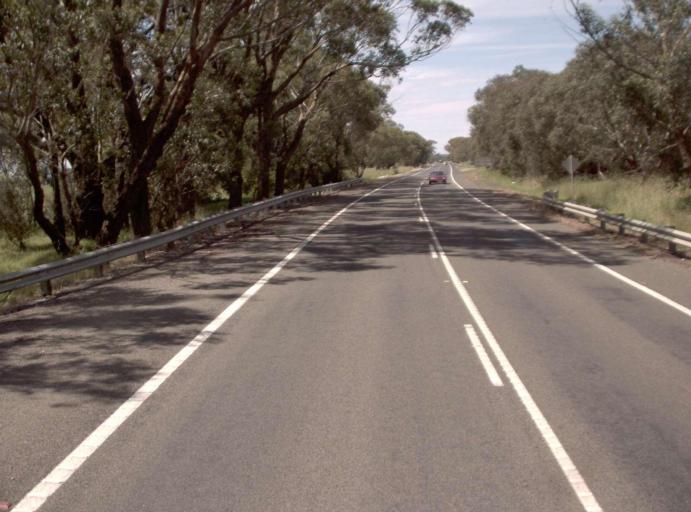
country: AU
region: Victoria
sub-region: Wellington
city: Sale
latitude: -37.9877
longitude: 147.0674
